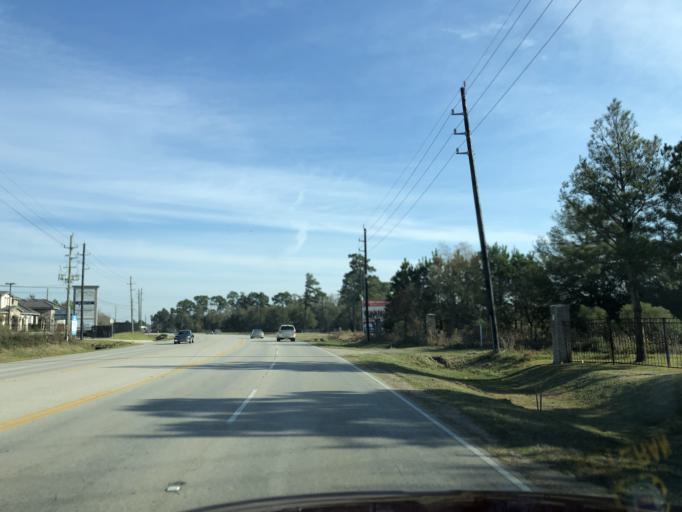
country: US
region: Texas
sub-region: Harris County
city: Tomball
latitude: 30.0383
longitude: -95.5482
